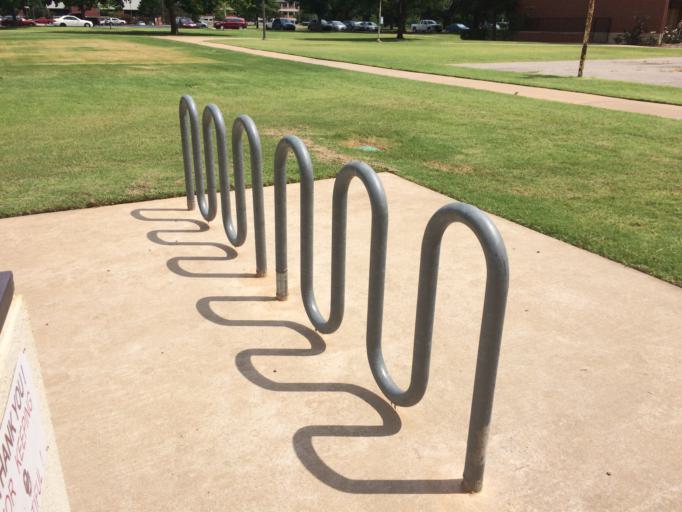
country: US
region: Oklahoma
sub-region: Cleveland County
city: Norman
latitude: 35.1990
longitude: -97.4429
